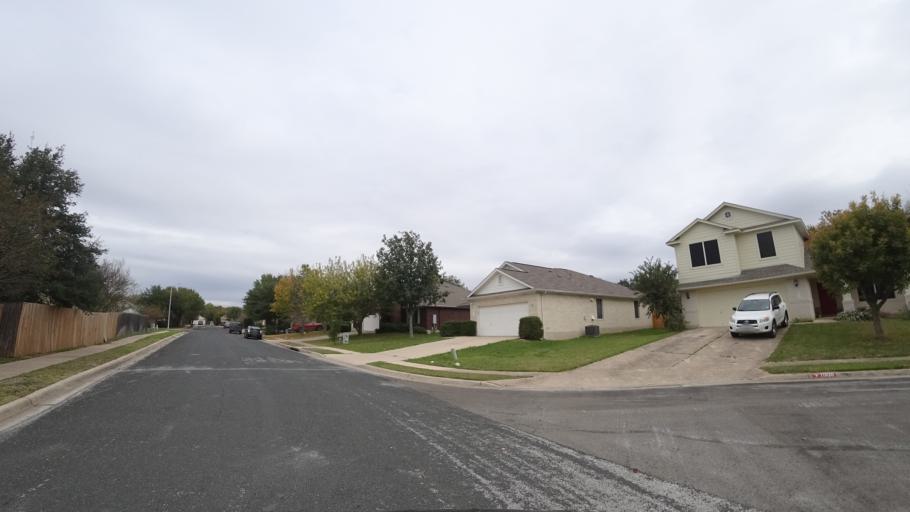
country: US
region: Texas
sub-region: Travis County
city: Shady Hollow
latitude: 30.1517
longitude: -97.8495
